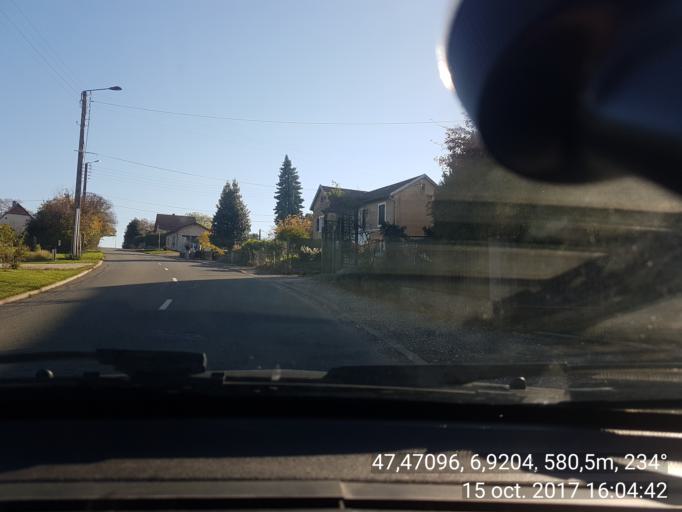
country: FR
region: Franche-Comte
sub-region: Territoire de Belfort
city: Beaucourt
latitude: 47.4708
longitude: 6.9203
